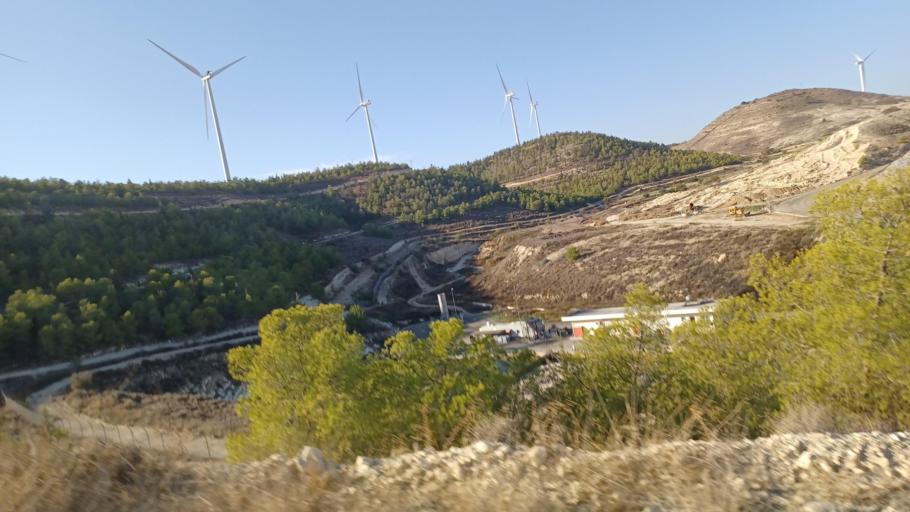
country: CY
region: Larnaka
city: Psevdas
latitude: 34.9613
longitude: 33.5139
